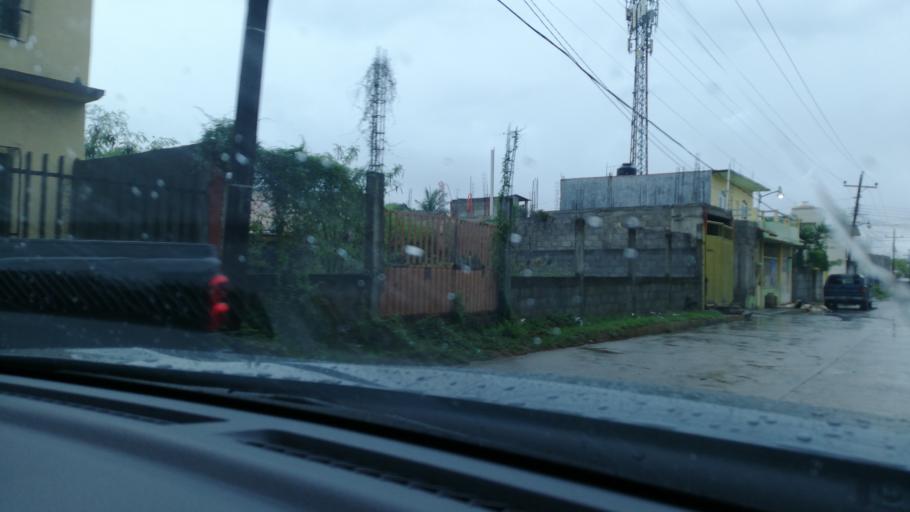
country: MX
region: Oaxaca
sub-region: Salina Cruz
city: Salina Cruz
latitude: 16.2052
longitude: -95.1961
